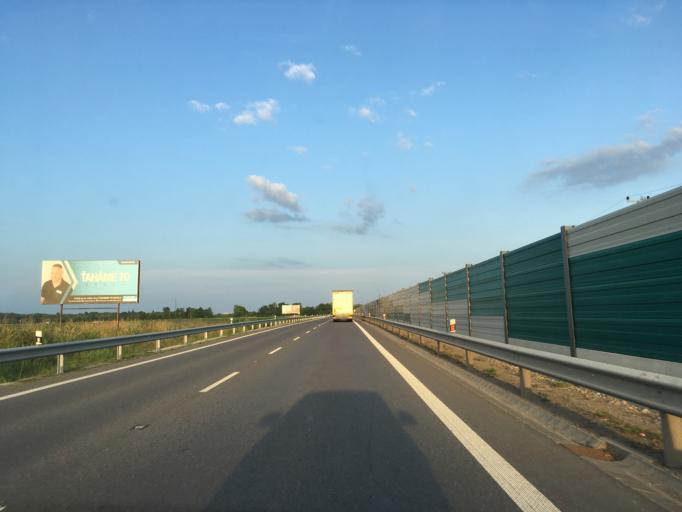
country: SK
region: Trnavsky
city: Sladkovicovo
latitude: 48.2067
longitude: 17.6537
